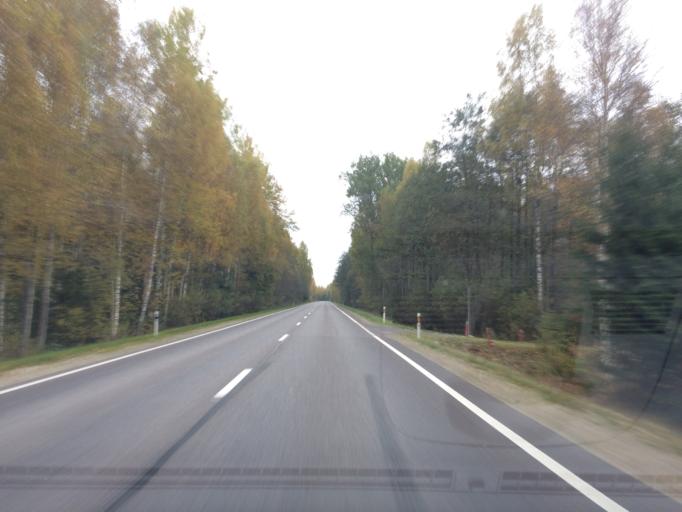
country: LV
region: Livani
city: Livani
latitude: 56.5277
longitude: 26.1531
